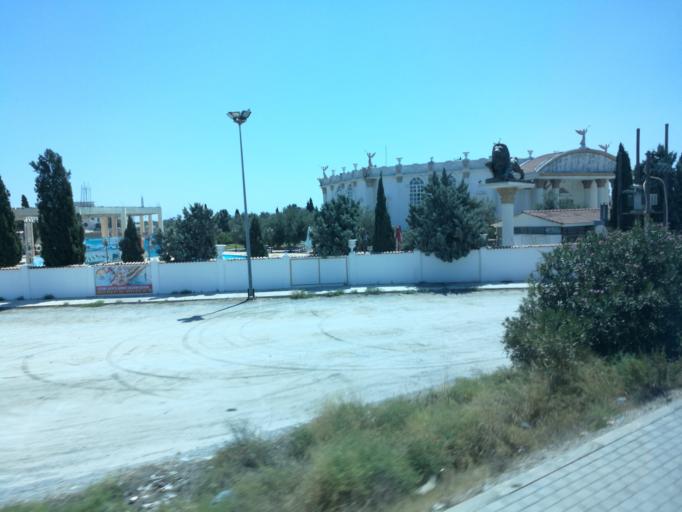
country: CY
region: Ammochostos
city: Famagusta
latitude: 35.1640
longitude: 33.9004
